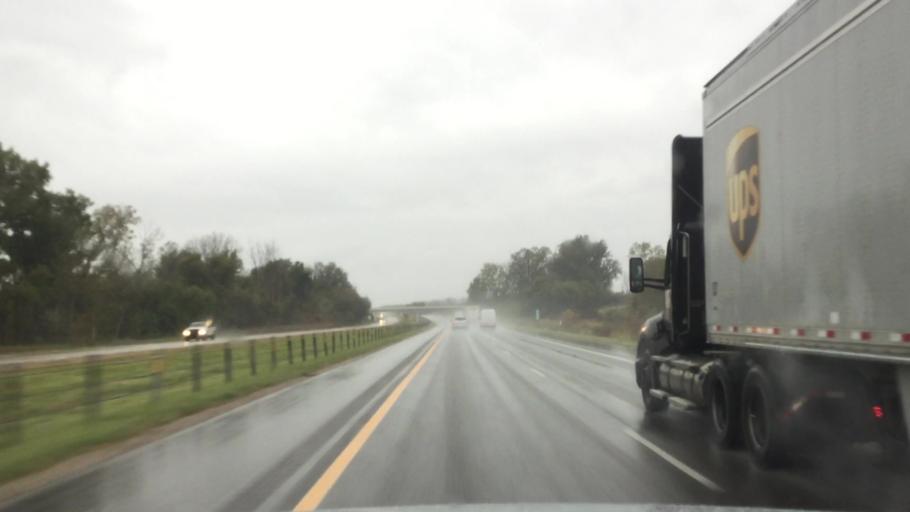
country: US
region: Michigan
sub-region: Van Buren County
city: Hartford
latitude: 42.1938
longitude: -86.1412
